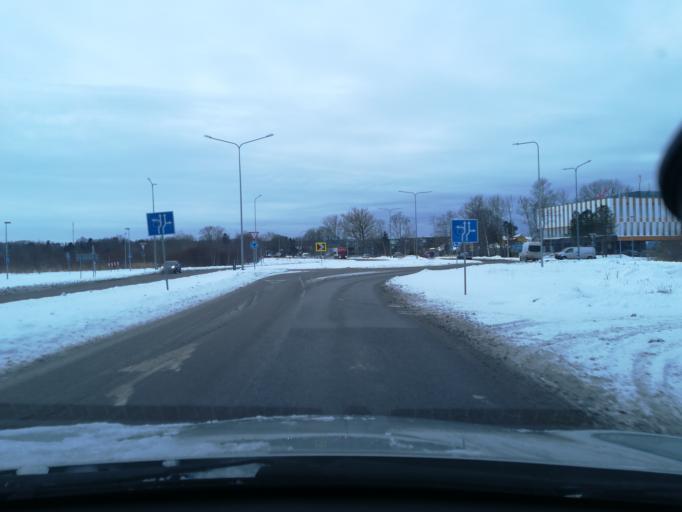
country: EE
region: Harju
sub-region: Harku vald
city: Tabasalu
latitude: 59.4371
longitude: 24.5742
